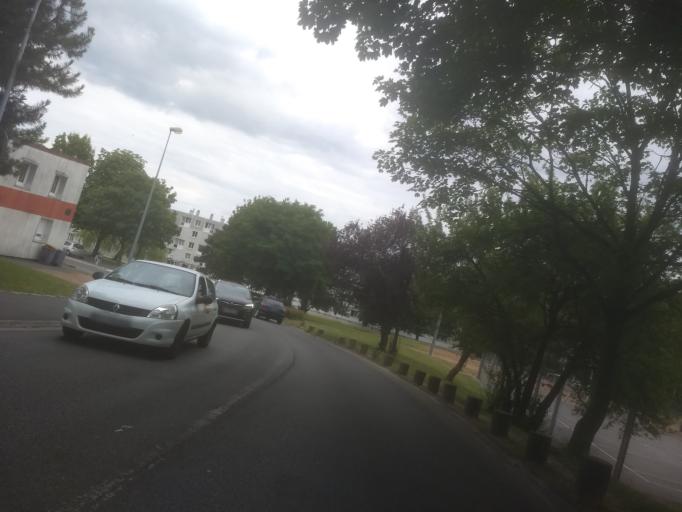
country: FR
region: Nord-Pas-de-Calais
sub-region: Departement du Pas-de-Calais
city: Anzin-Saint-Aubin
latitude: 50.2958
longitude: 2.7410
